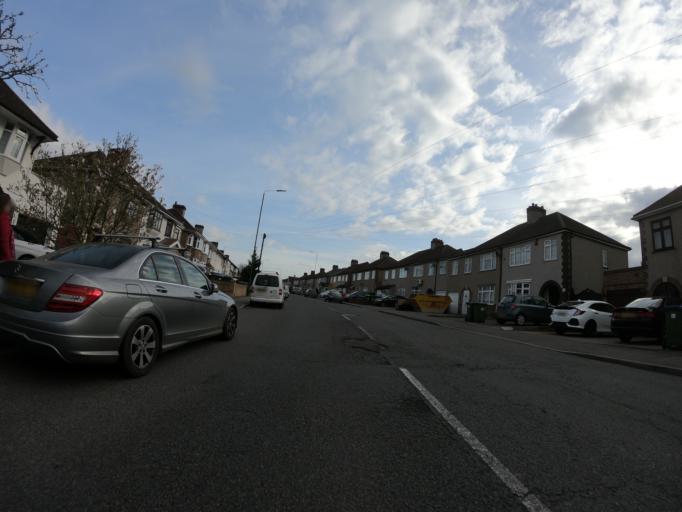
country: GB
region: England
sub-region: Greater London
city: Bexleyheath
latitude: 51.4756
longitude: 0.1446
